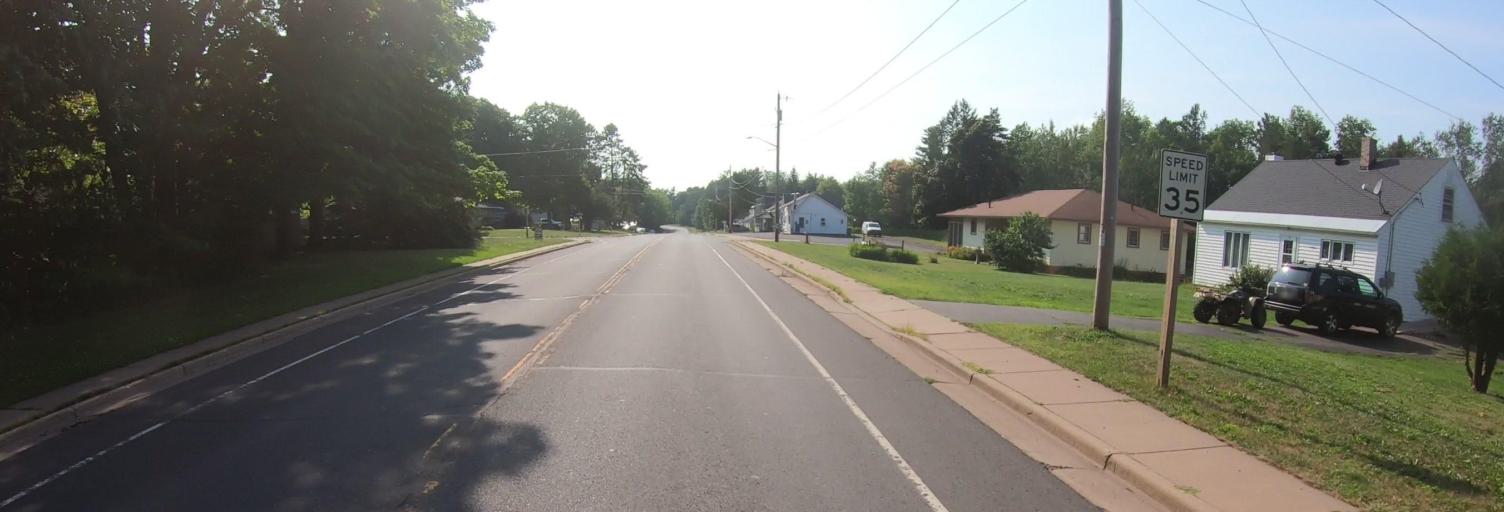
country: US
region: Wisconsin
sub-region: Iron County
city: Hurley
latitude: 46.4273
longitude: -90.2502
